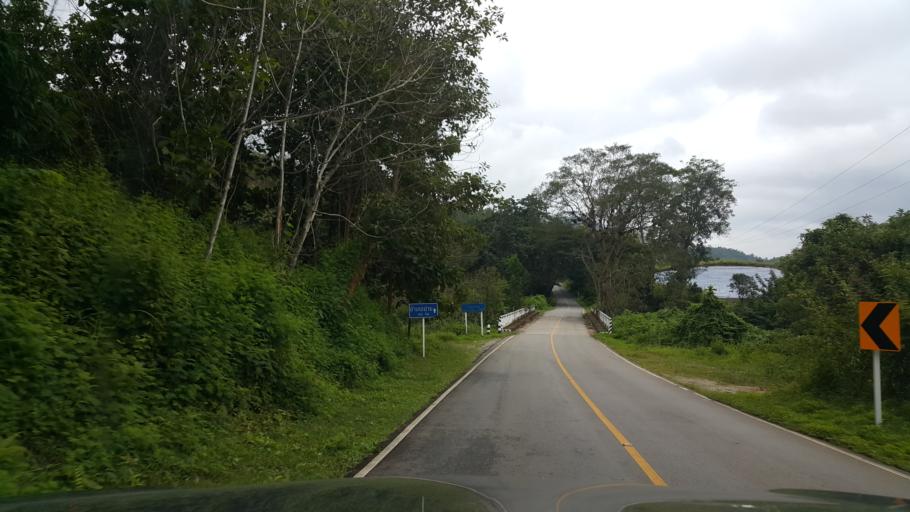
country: TH
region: Chiang Mai
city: Samoeng
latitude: 18.8604
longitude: 98.6476
